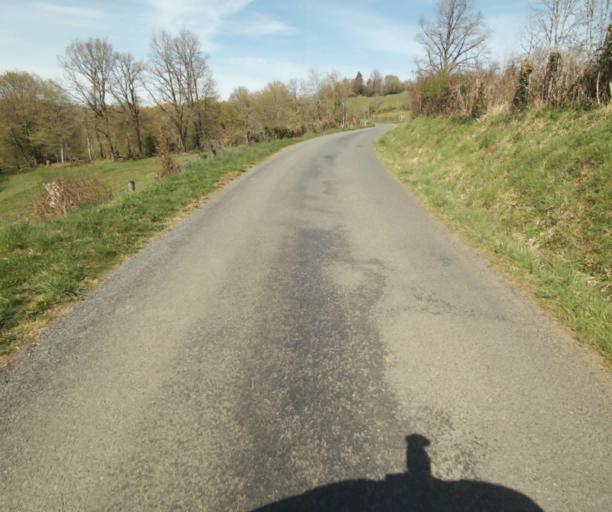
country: FR
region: Limousin
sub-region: Departement de la Correze
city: Naves
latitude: 45.3517
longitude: 1.7781
